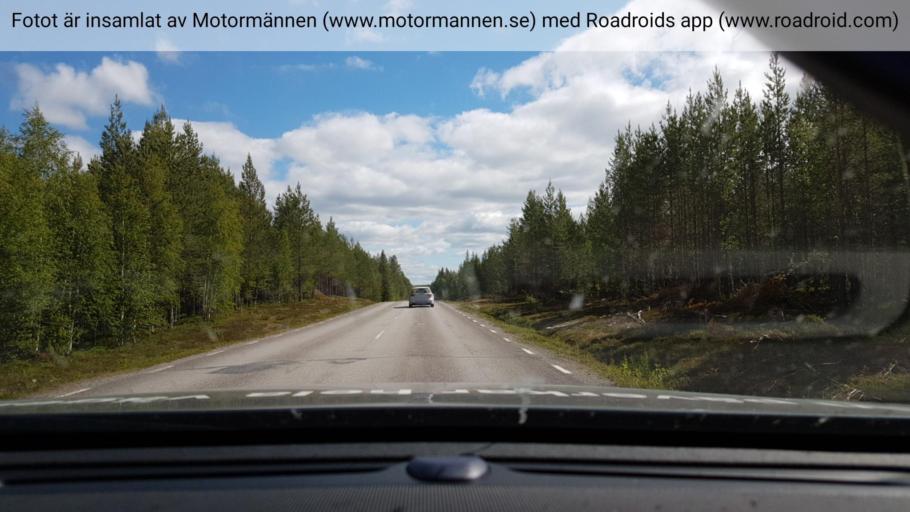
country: SE
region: Vaesterbotten
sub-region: Sorsele Kommun
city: Sorsele
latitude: 65.5862
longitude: 17.5120
